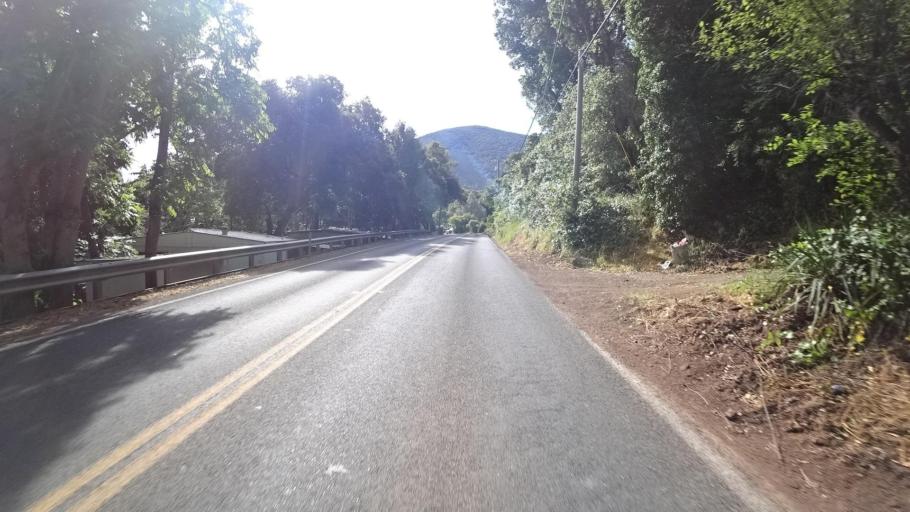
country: US
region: California
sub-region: Lake County
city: Soda Bay
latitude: 39.0015
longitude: -122.7946
